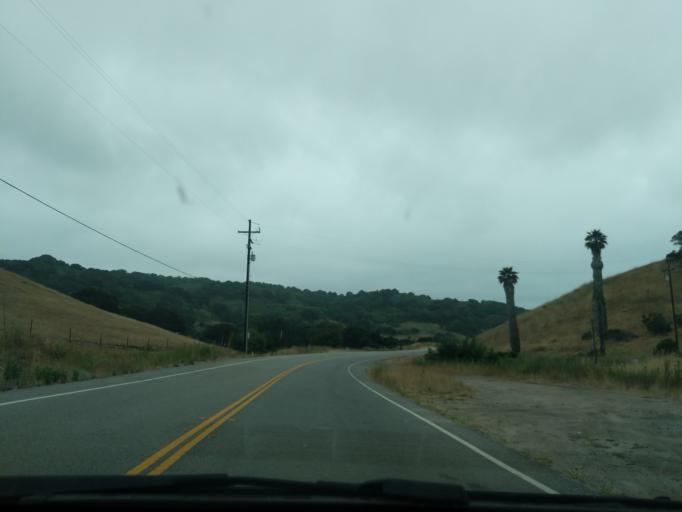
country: US
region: California
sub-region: San Benito County
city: Aromas
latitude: 36.8632
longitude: -121.6223
